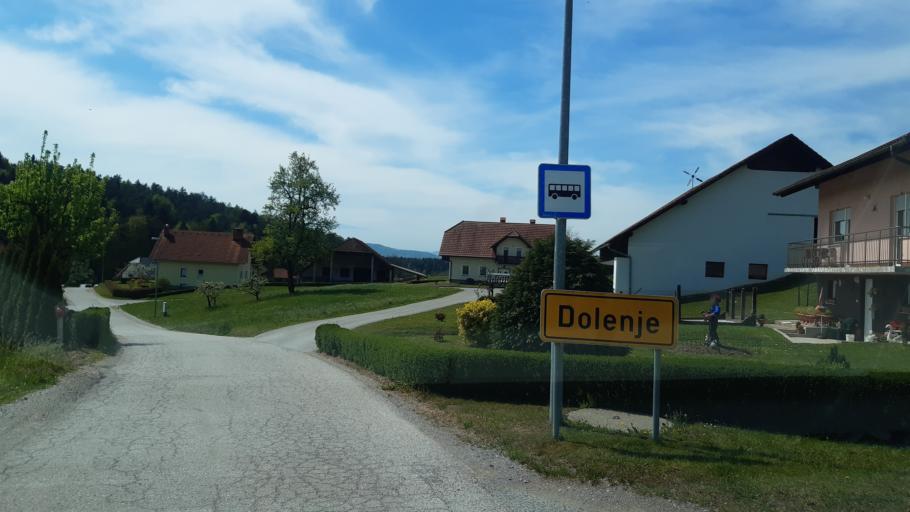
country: SI
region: Lukovica
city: Lukovica pri Domzalah
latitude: 46.1771
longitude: 14.6582
